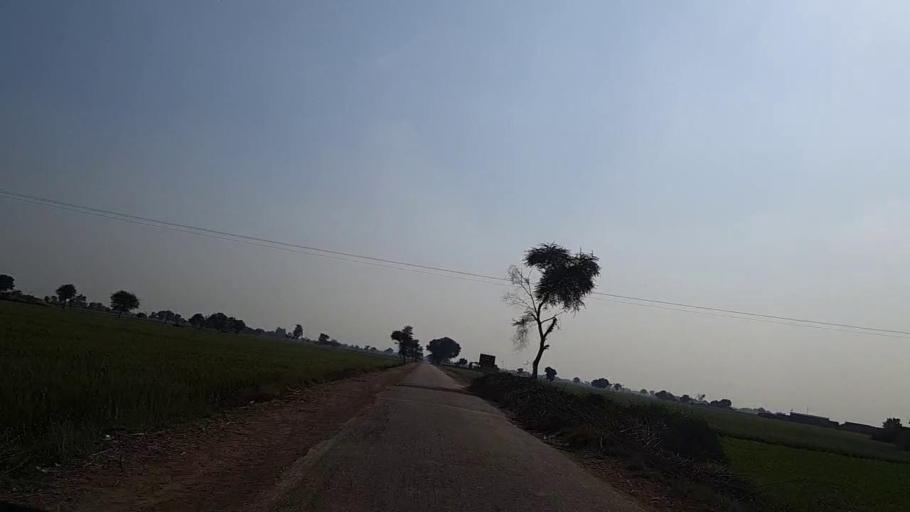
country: PK
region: Sindh
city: Sakrand
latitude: 26.0939
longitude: 68.2904
